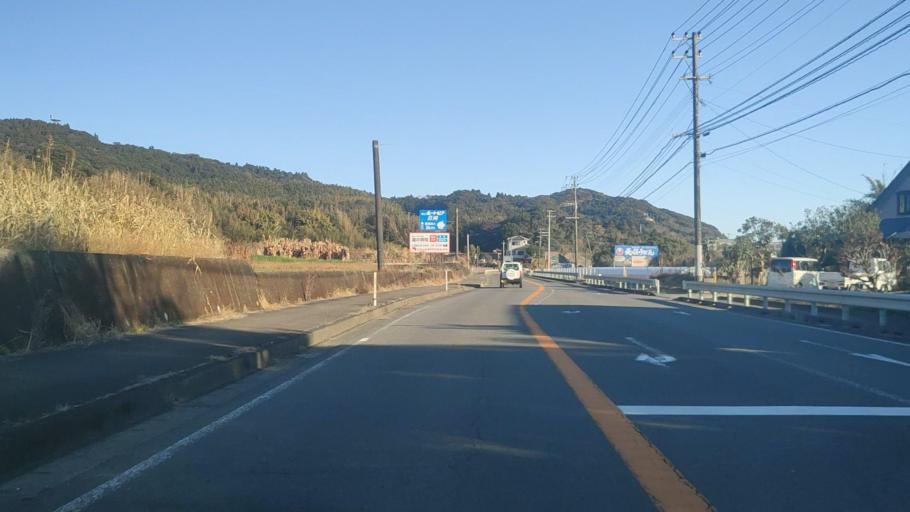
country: JP
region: Miyazaki
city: Nobeoka
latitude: 32.3625
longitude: 131.6229
